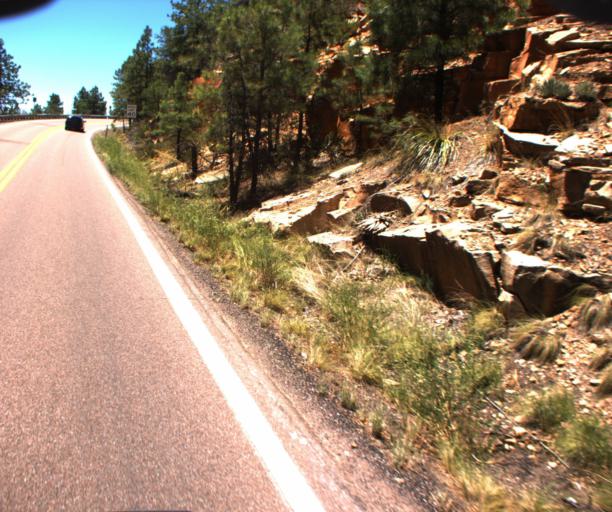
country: US
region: Arizona
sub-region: Gila County
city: Pine
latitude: 34.4215
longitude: -111.5019
